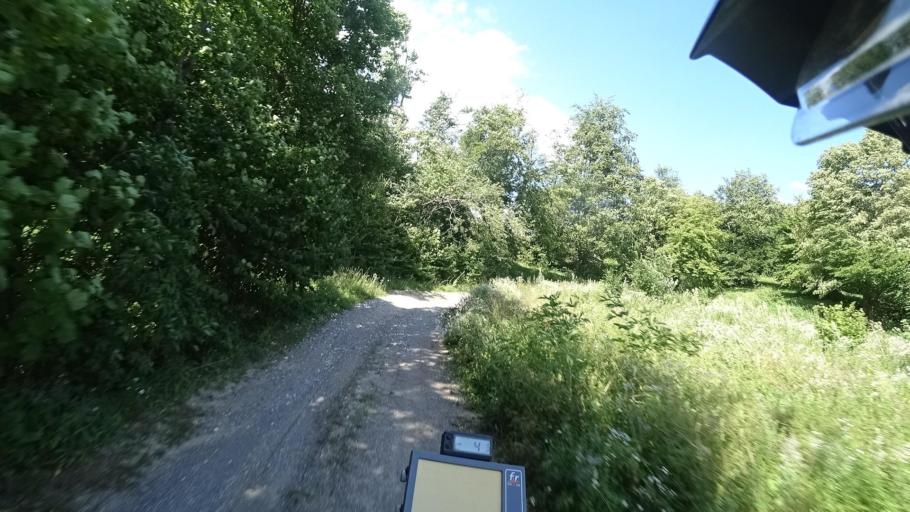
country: HR
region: Karlovacka
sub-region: Grad Ogulin
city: Ogulin
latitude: 45.1757
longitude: 15.1257
